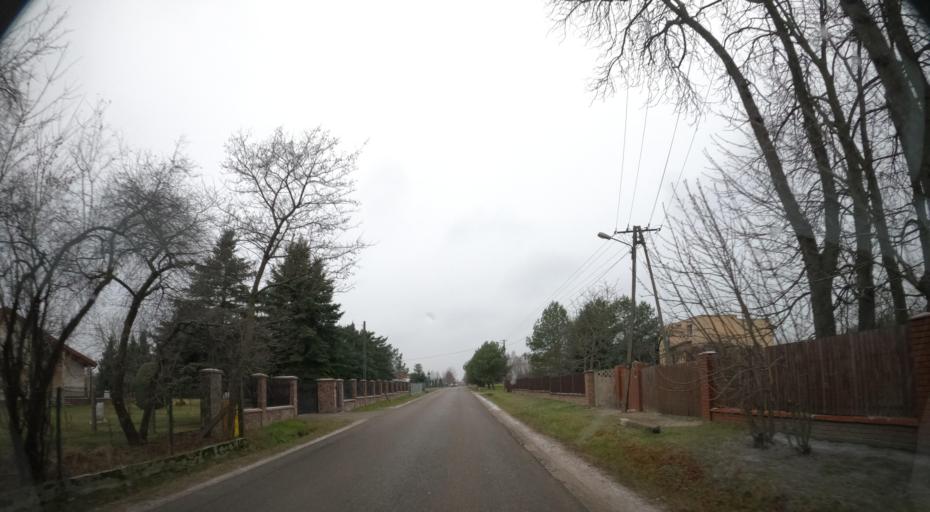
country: PL
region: Masovian Voivodeship
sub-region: Powiat radomski
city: Skaryszew
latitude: 51.3791
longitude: 21.2462
